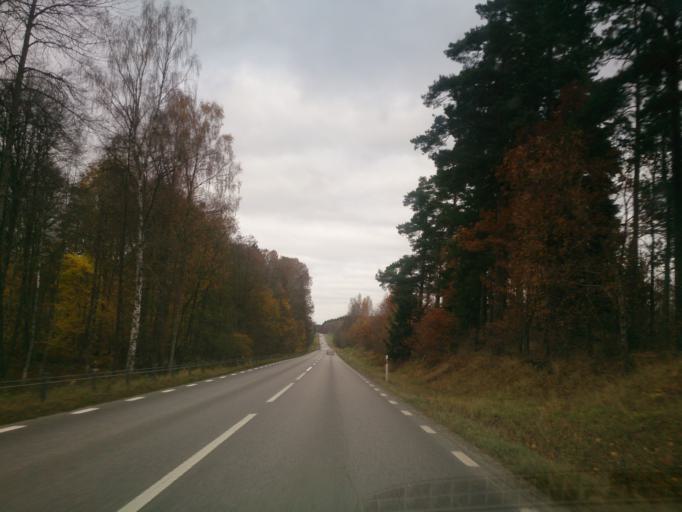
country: SE
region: OEstergoetland
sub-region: Atvidabergs Kommun
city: Atvidaberg
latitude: 58.2715
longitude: 15.9209
